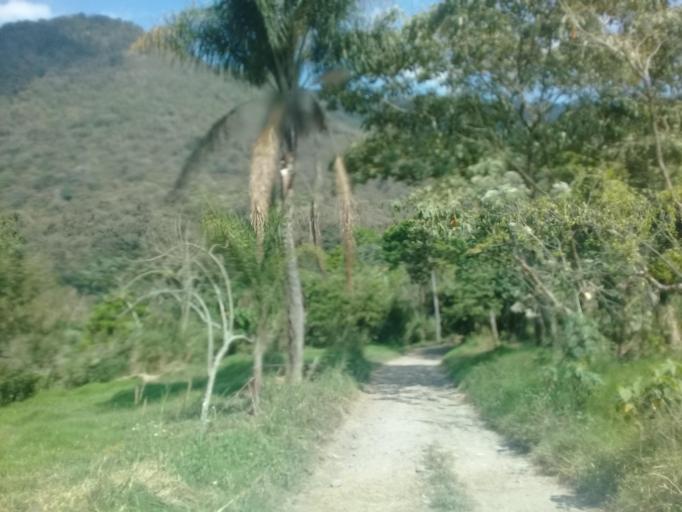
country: MX
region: Veracruz
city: Jalapilla
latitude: 18.8293
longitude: -97.0701
